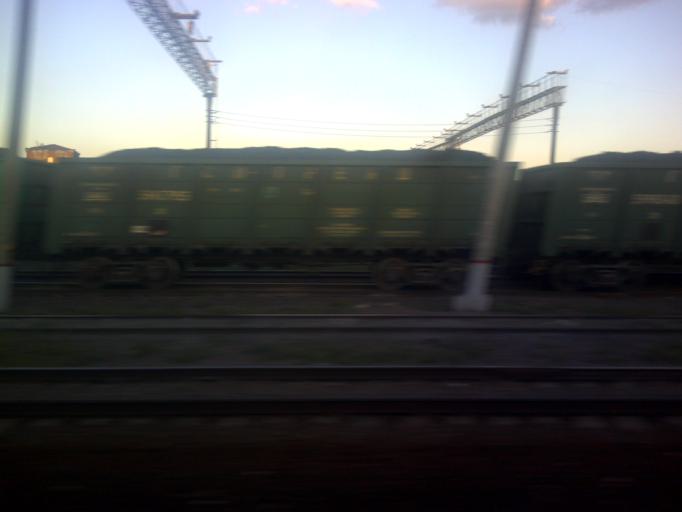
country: RU
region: Moscow
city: Mar'ino
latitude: 55.6698
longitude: 37.7258
